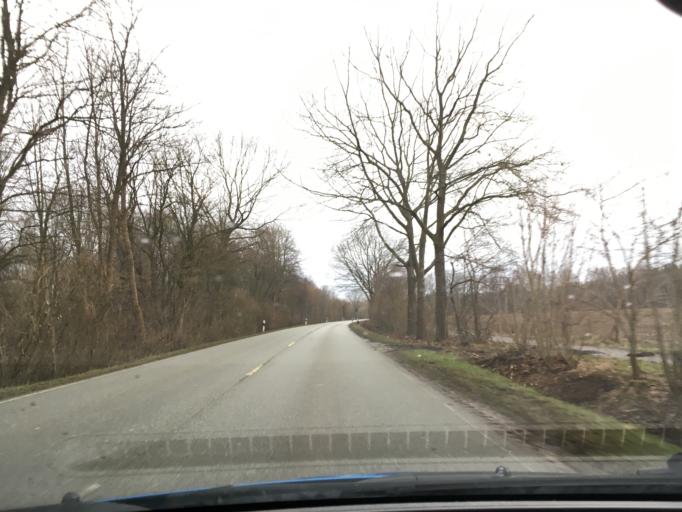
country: DE
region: Schleswig-Holstein
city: Siebeneichen
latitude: 53.4958
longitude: 10.6130
